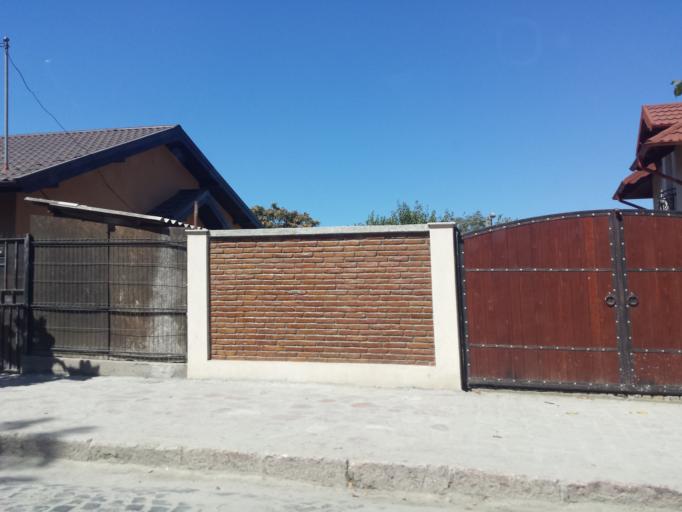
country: RO
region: Tulcea
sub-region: Municipiul Tulcea
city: Tulcea
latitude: 45.1821
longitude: 28.8090
